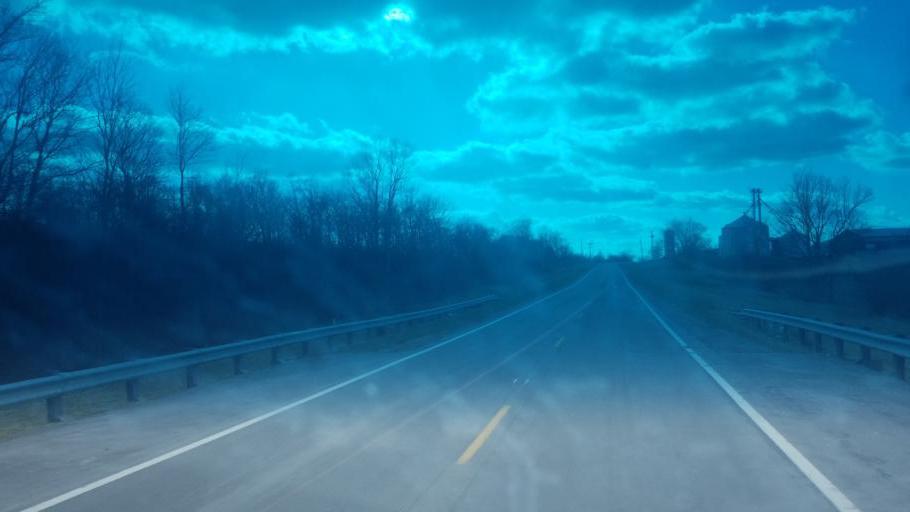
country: US
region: Ohio
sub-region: Highland County
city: Greenfield
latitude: 39.3464
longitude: -83.4137
